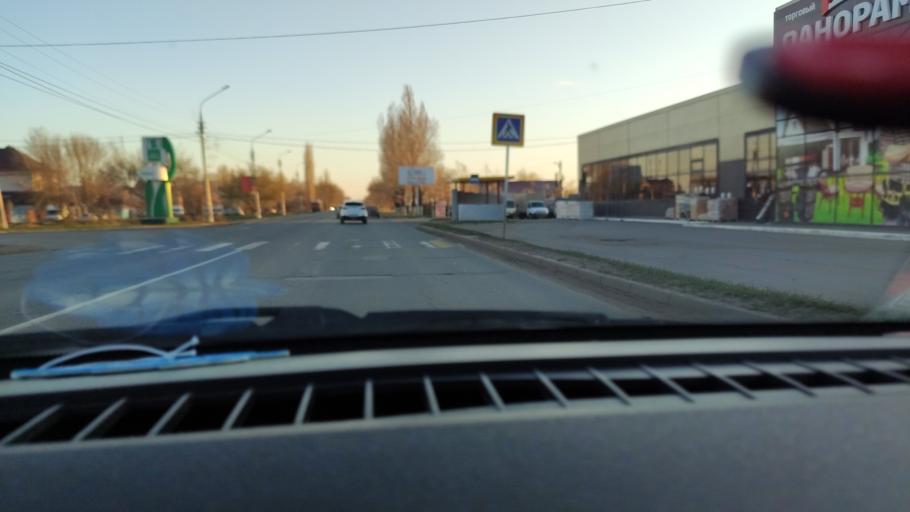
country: RU
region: Saratov
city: Engel's
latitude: 51.4577
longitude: 46.0886
